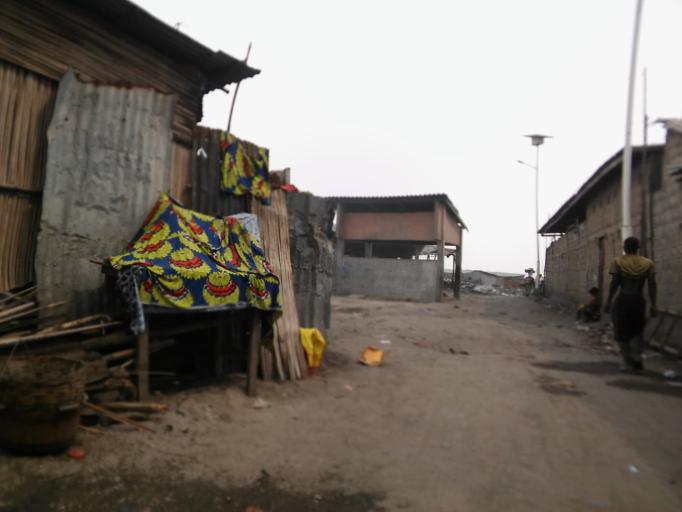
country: BJ
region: Littoral
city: Cotonou
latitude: 6.3883
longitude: 2.4215
